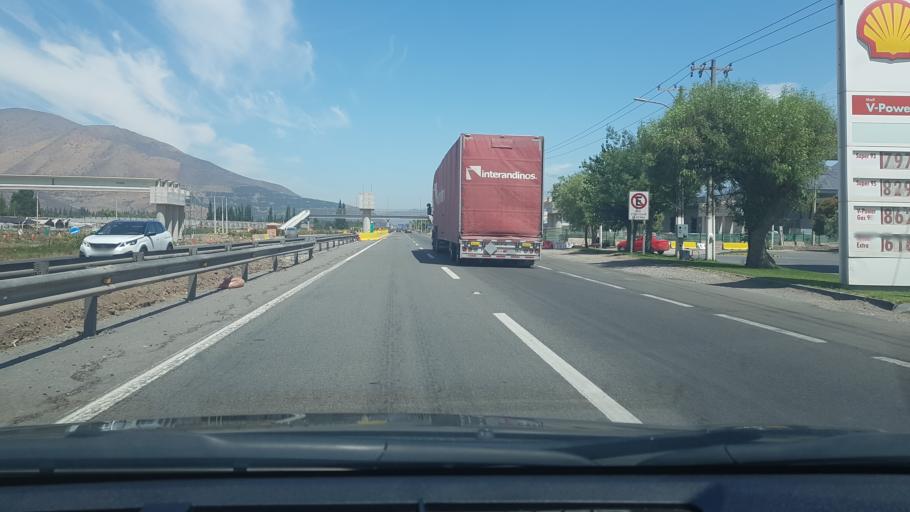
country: CL
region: Valparaiso
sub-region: Provincia de San Felipe
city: Llaillay
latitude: -32.8484
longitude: -70.9591
